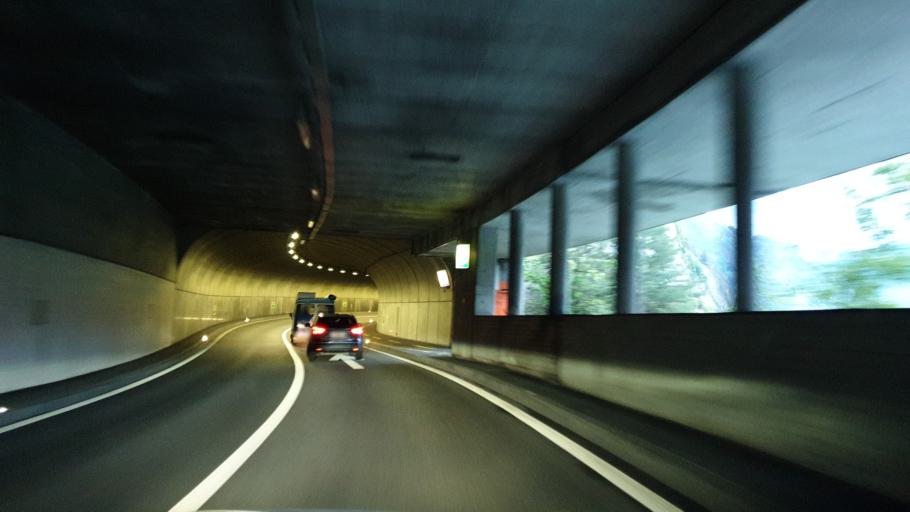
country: CH
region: Schwyz
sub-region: Bezirk Schwyz
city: Ingenbohl
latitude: 46.9703
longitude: 8.6124
